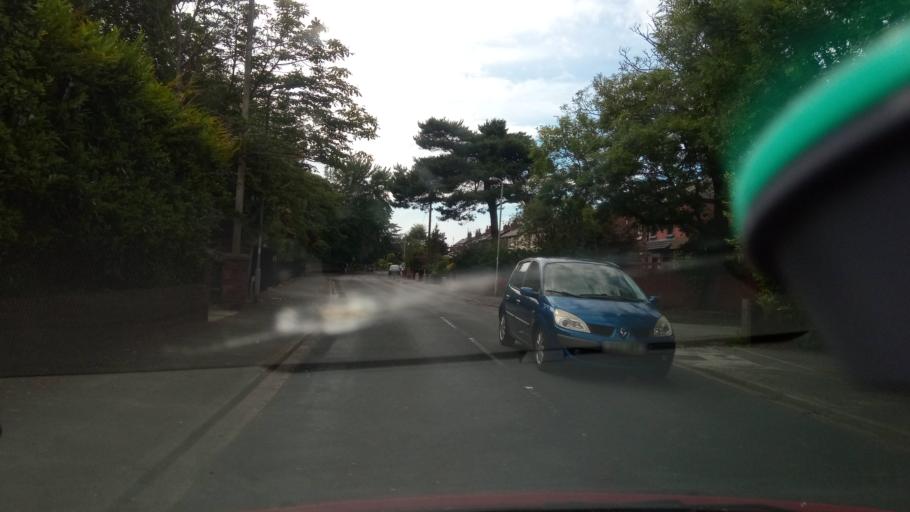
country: GB
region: England
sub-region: Sefton
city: Formby
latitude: 53.5509
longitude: -3.0588
